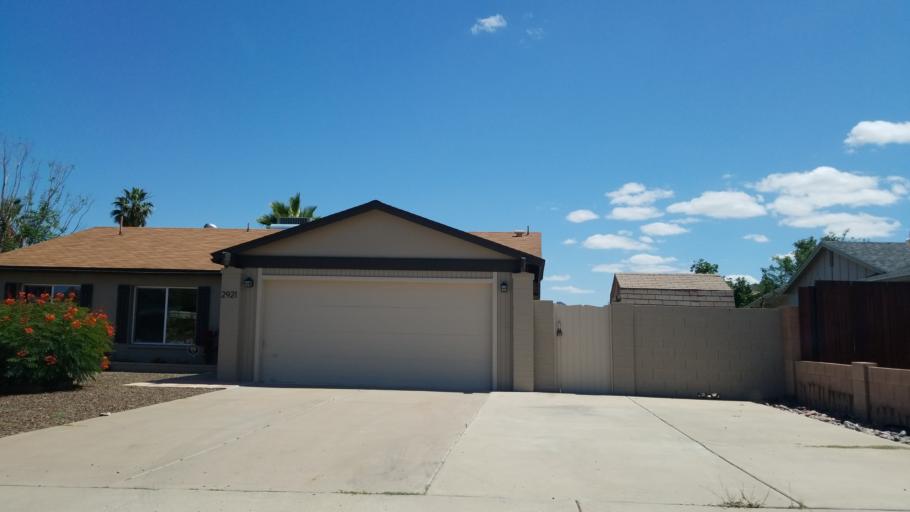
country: US
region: Arizona
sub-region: Maricopa County
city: Paradise Valley
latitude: 33.6078
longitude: -112.0189
